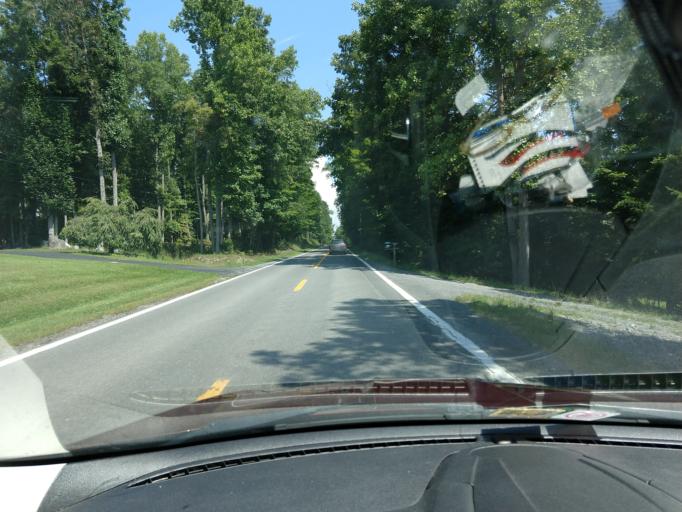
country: US
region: West Virginia
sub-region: Greenbrier County
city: Fairlea
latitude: 37.8324
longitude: -80.5566
